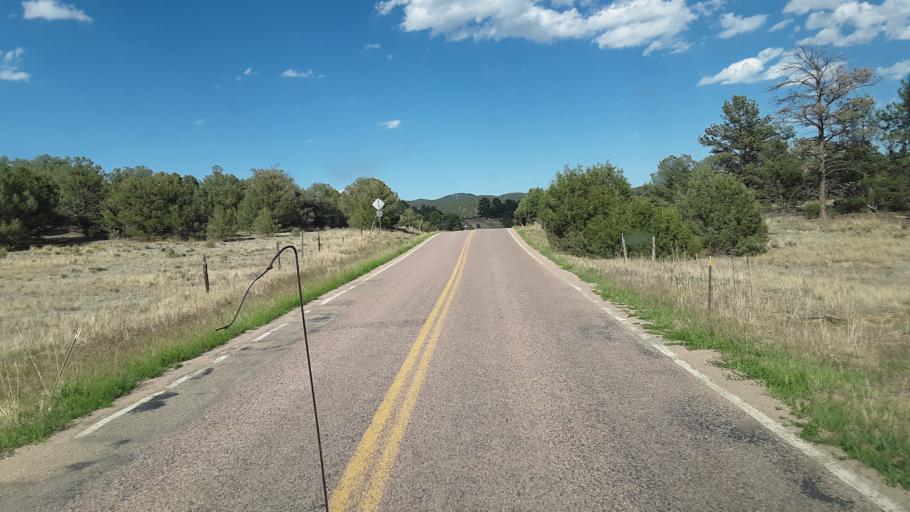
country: US
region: Colorado
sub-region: Custer County
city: Westcliffe
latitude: 38.3558
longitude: -105.4790
